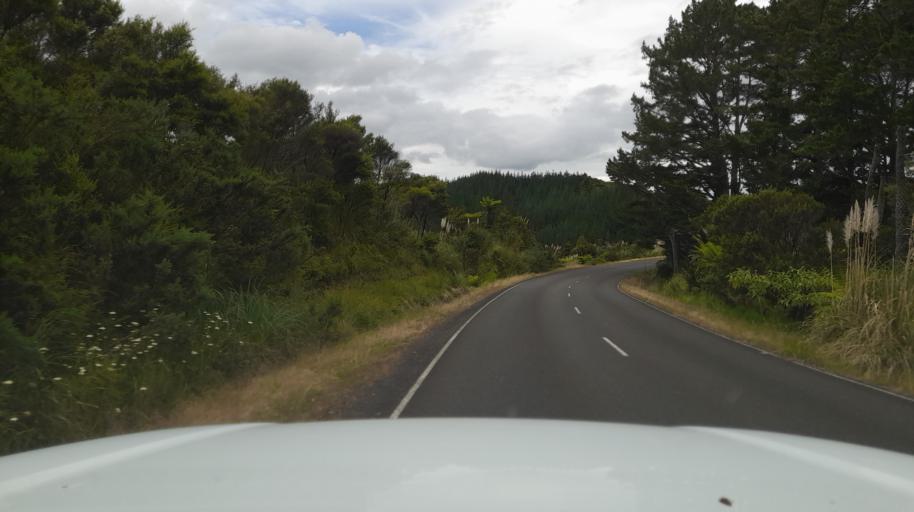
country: NZ
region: Northland
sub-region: Far North District
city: Kaitaia
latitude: -35.3699
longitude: 173.4184
